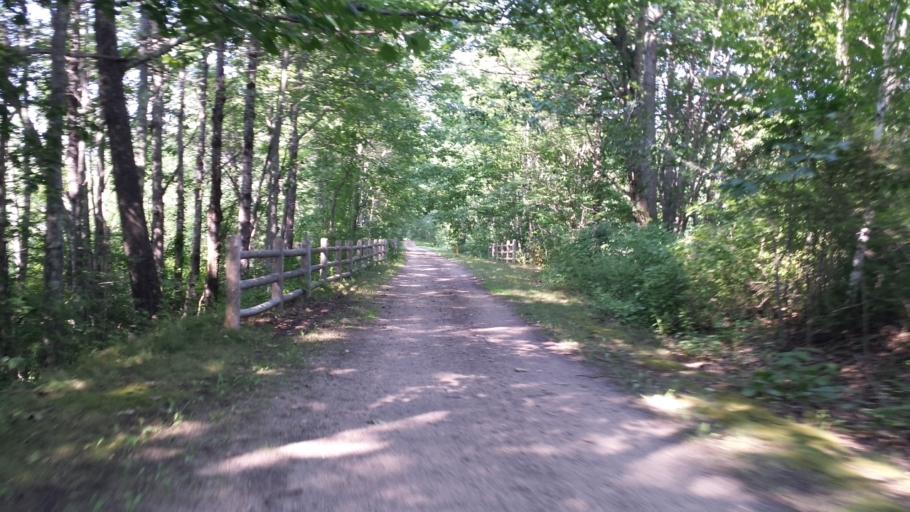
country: US
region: Maine
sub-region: York County
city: Biddeford
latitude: 43.4591
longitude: -70.5051
